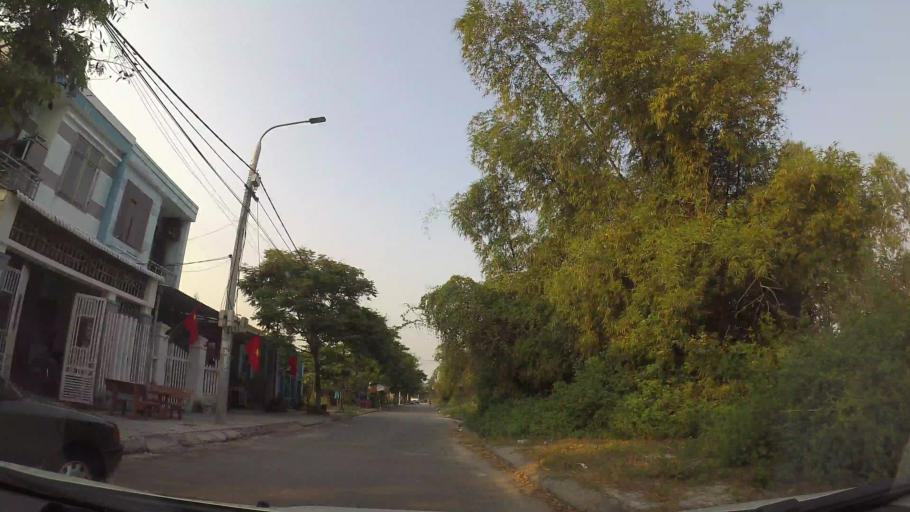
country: VN
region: Da Nang
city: Ngu Hanh Son
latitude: 15.9845
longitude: 108.2538
